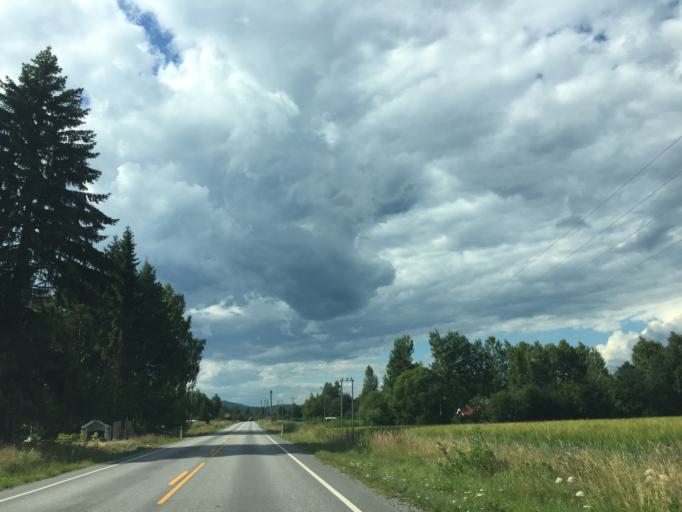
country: NO
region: Hedmark
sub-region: Sor-Odal
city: Skarnes
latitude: 60.2446
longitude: 11.7088
